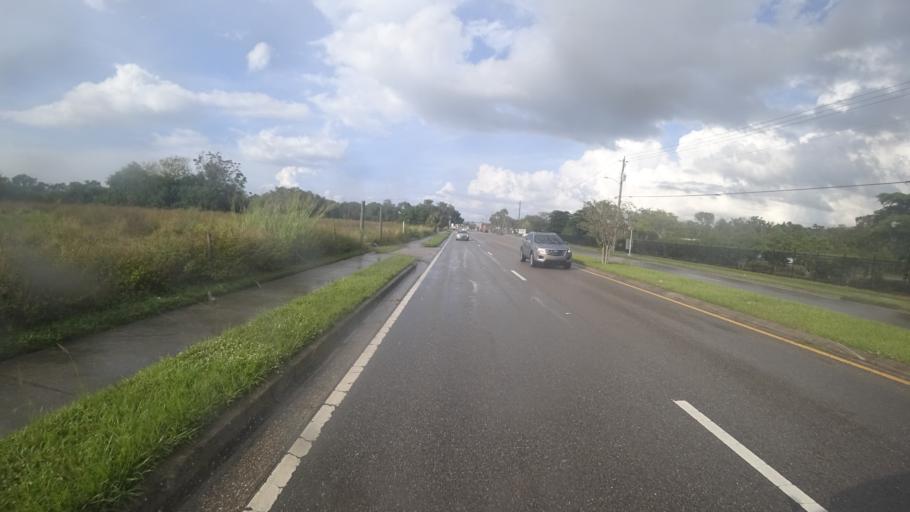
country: US
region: Florida
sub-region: Manatee County
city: Memphis
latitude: 27.5184
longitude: -82.5526
